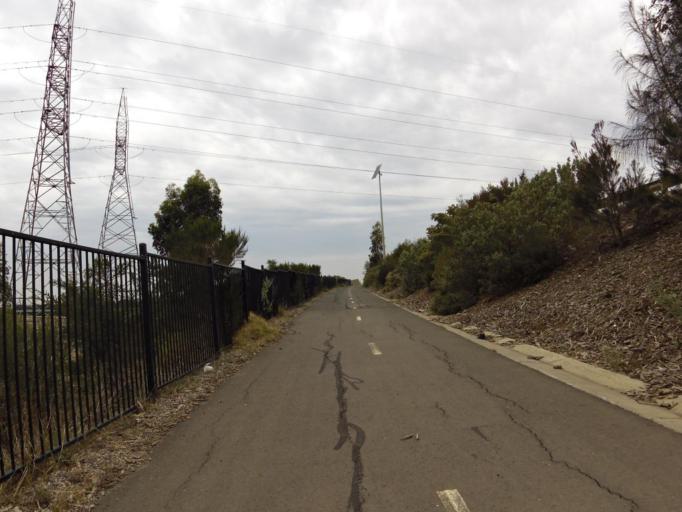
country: AU
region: Victoria
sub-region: Melton
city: Caroline Springs
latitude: -37.7690
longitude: 144.7453
